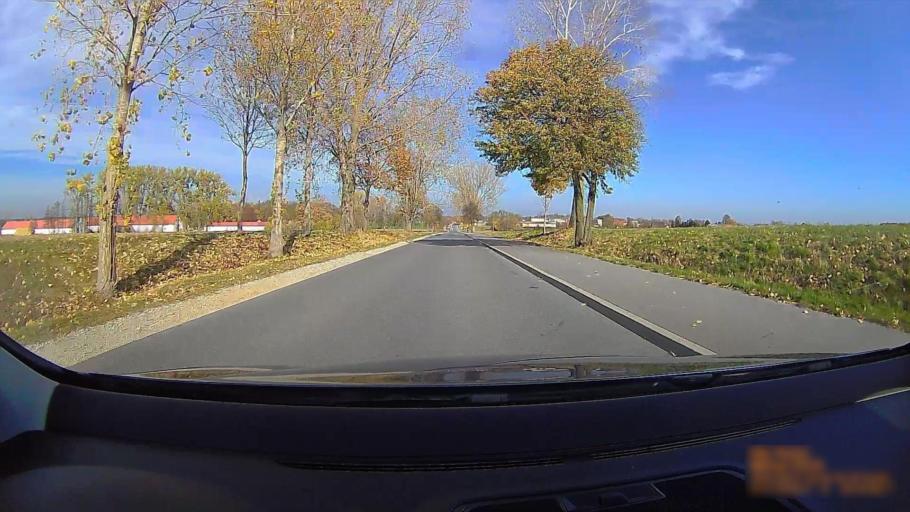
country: PL
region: Greater Poland Voivodeship
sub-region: Powiat kepinski
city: Kepno
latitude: 51.3415
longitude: 18.0225
